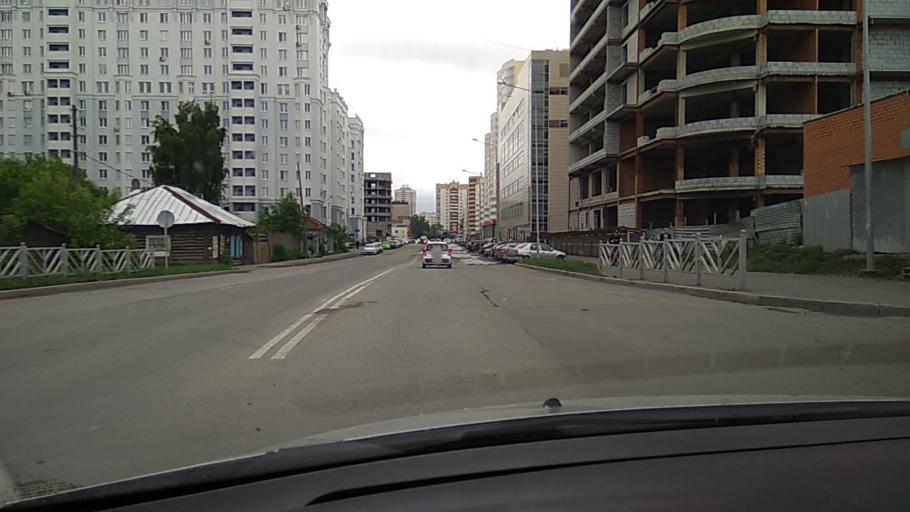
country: RU
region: Sverdlovsk
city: Yekaterinburg
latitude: 56.8080
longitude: 60.6134
